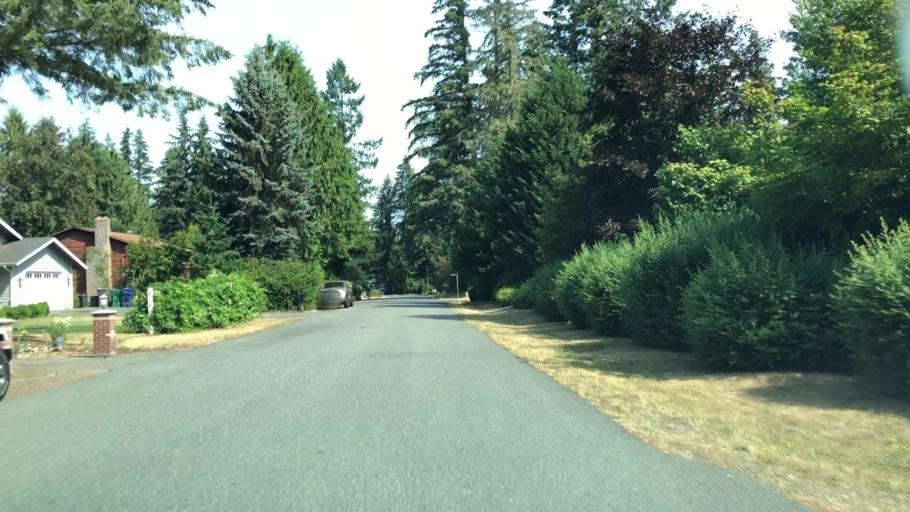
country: US
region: Washington
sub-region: King County
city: Cottage Lake
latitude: 47.7408
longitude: -122.0874
